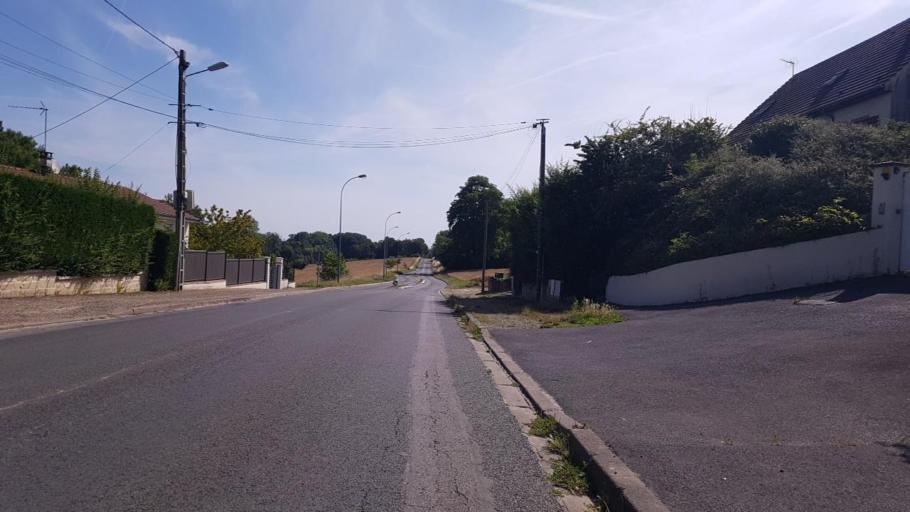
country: FR
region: Picardie
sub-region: Departement de l'Oise
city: Pontpoint
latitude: 49.3031
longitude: 2.6609
